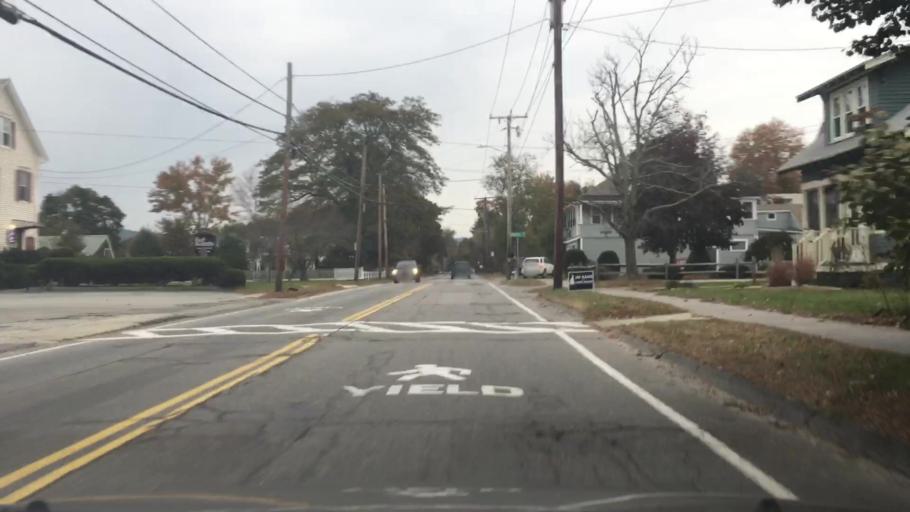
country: US
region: New Hampshire
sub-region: Cheshire County
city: Keene
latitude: 42.9354
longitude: -72.3016
